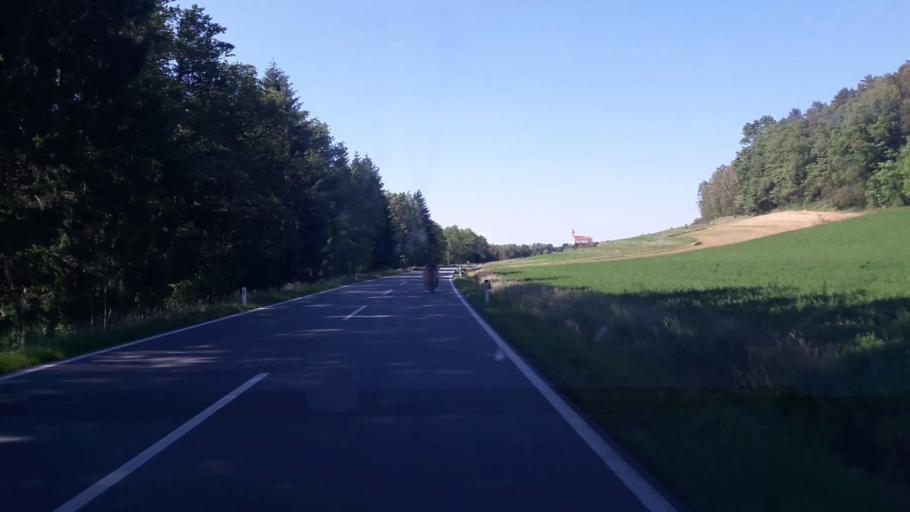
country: AT
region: Burgenland
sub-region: Politischer Bezirk Oberwart
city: Litzelsdorf
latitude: 47.1959
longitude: 16.1606
